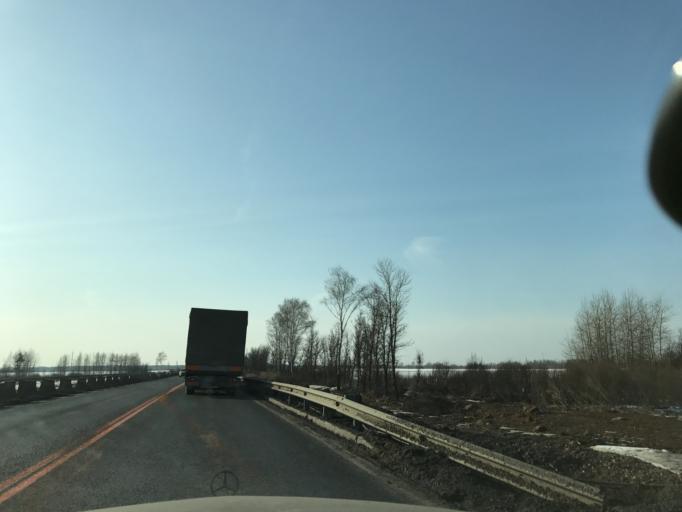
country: RU
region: Vladimir
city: Novovyazniki
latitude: 56.2177
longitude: 42.2187
